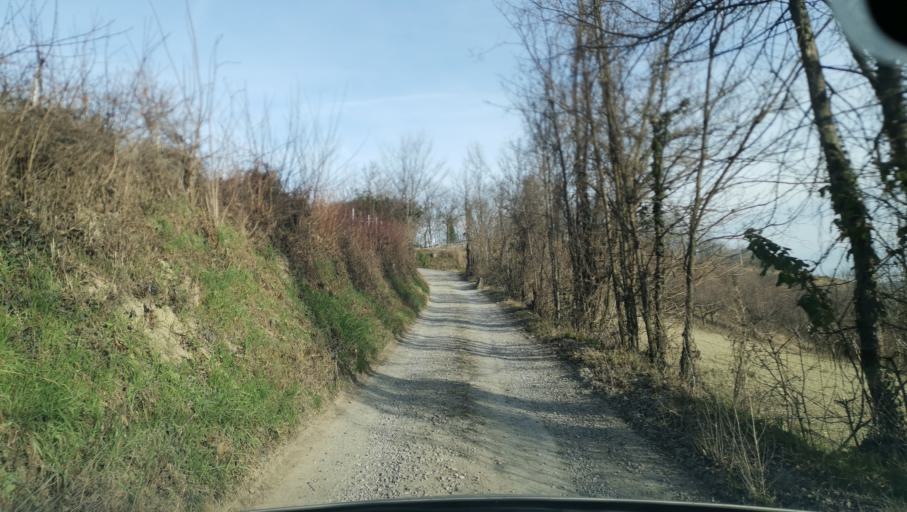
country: IT
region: Piedmont
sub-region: Provincia di Torino
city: Gassino Torinese
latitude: 45.1082
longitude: 7.8278
